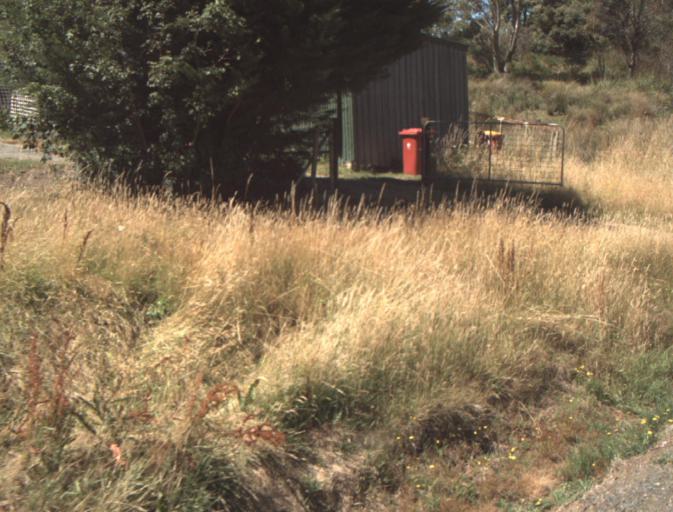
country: AU
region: Tasmania
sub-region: Launceston
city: Newstead
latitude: -41.3557
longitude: 147.3030
